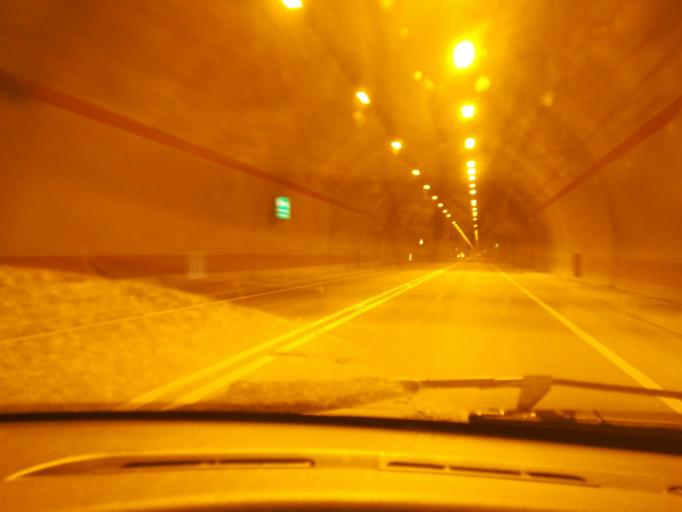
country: IT
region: The Marches
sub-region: Provincia di Macerata
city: Macerata
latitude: 43.2978
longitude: 13.4415
